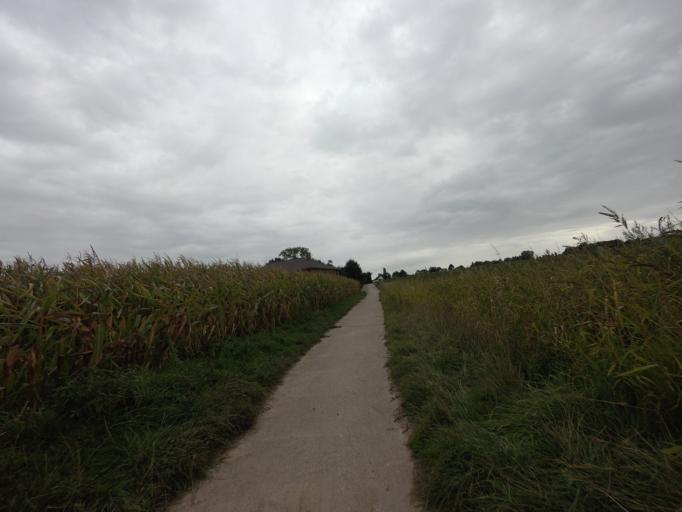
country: BE
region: Flanders
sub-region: Provincie Vlaams-Brabant
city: Meise
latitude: 50.9499
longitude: 4.3392
